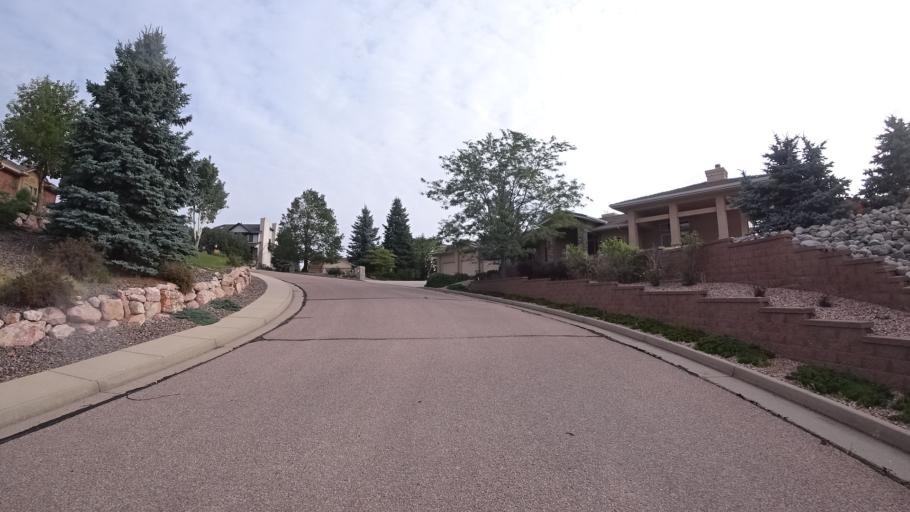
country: US
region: Colorado
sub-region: El Paso County
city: Air Force Academy
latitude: 38.9308
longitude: -104.8580
